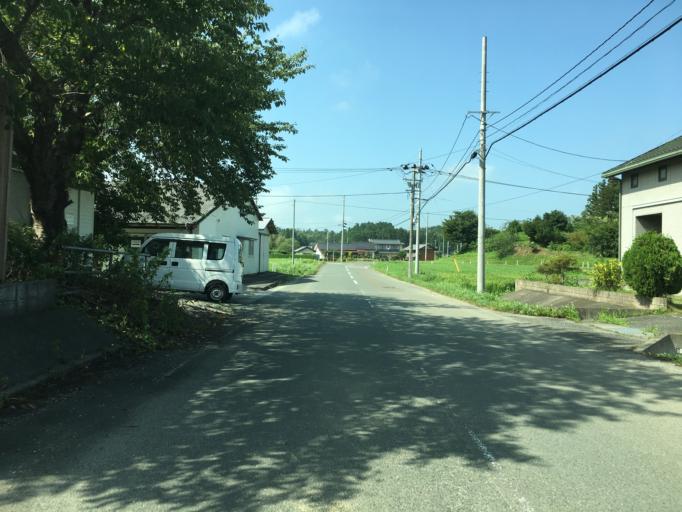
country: JP
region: Miyagi
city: Marumori
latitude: 37.8900
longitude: 140.8908
